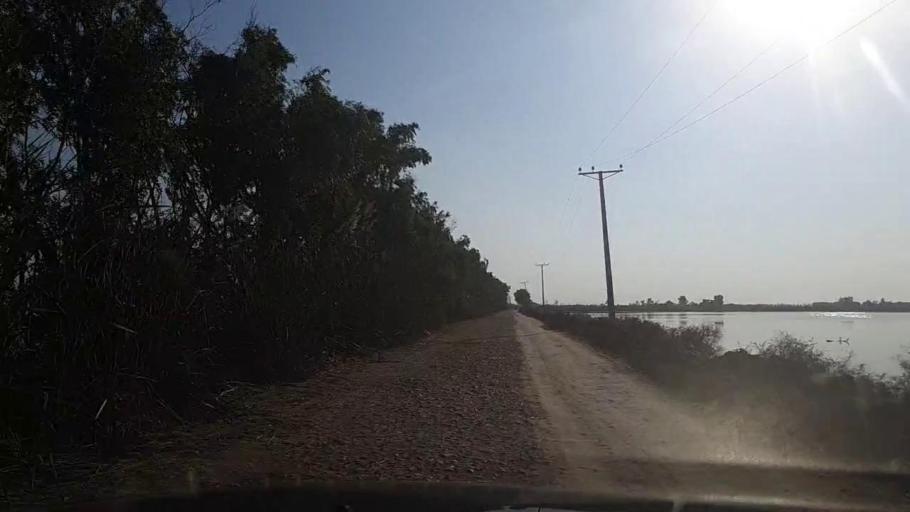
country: PK
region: Sindh
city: Gharo
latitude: 24.7211
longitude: 67.6907
